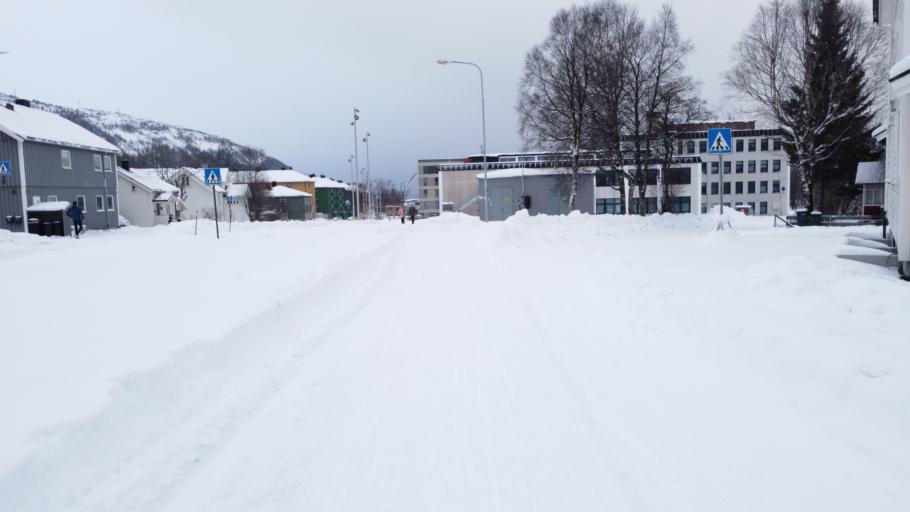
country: NO
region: Nordland
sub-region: Rana
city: Mo i Rana
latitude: 66.3124
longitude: 14.1491
